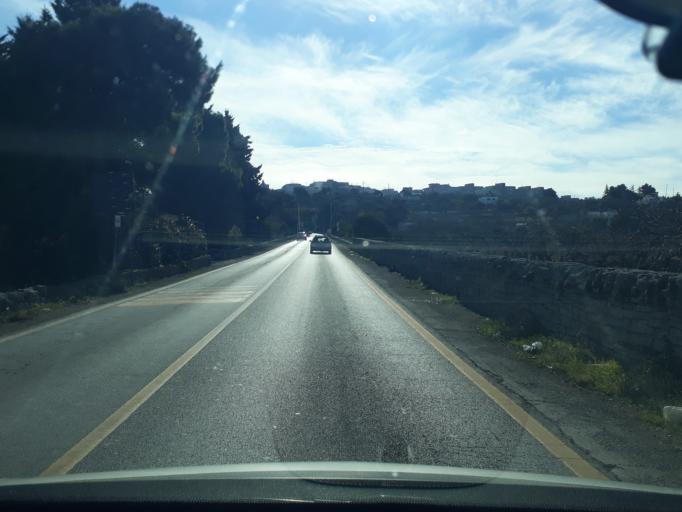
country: IT
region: Apulia
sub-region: Provincia di Taranto
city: Martina Franca
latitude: 40.7166
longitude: 17.3327
